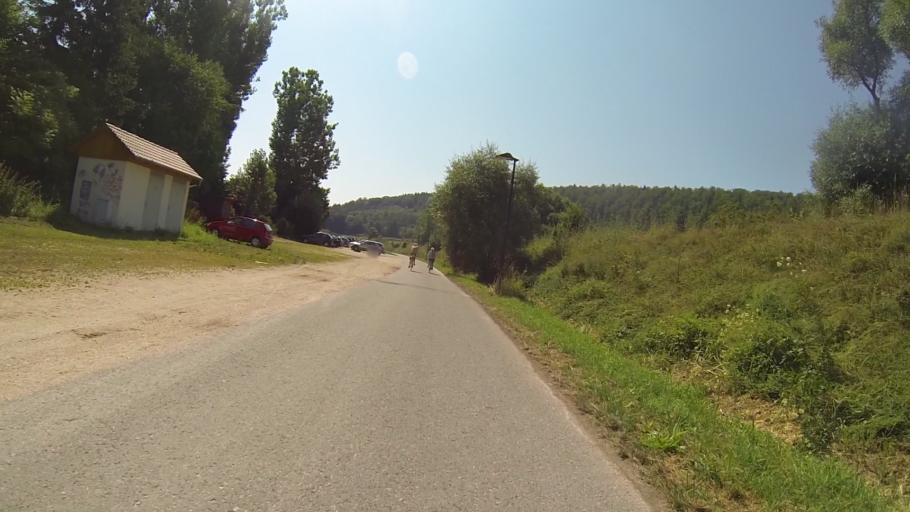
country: DE
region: Baden-Wuerttemberg
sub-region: Regierungsbezirk Stuttgart
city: Heidenheim an der Brenz
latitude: 48.7173
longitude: 10.1497
